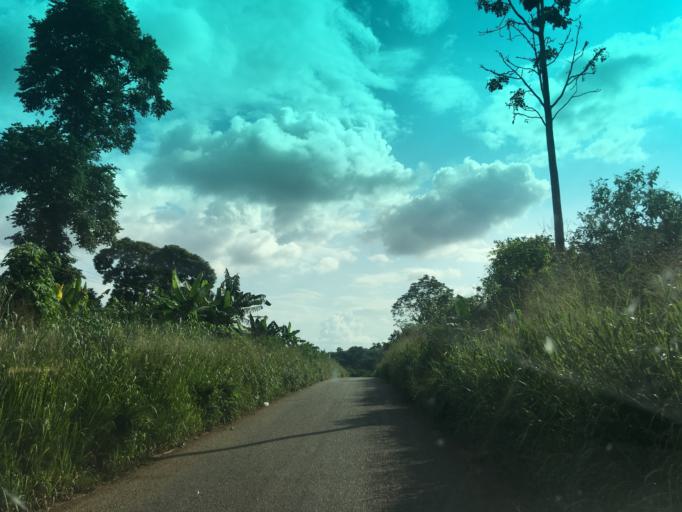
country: GH
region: Western
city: Bibiani
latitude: 6.7928
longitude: -2.5335
